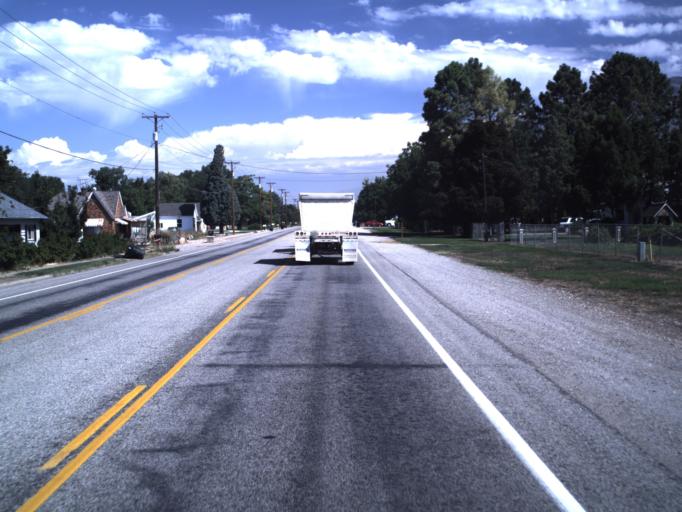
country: US
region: Utah
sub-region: Weber County
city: Farr West
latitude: 41.2987
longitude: -112.0277
